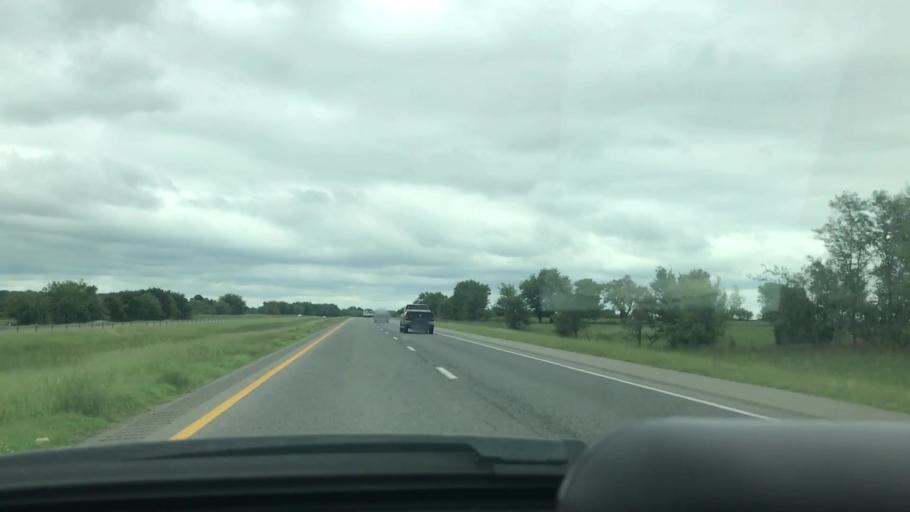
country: US
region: Oklahoma
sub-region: McIntosh County
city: Checotah
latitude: 35.4217
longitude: -95.5548
